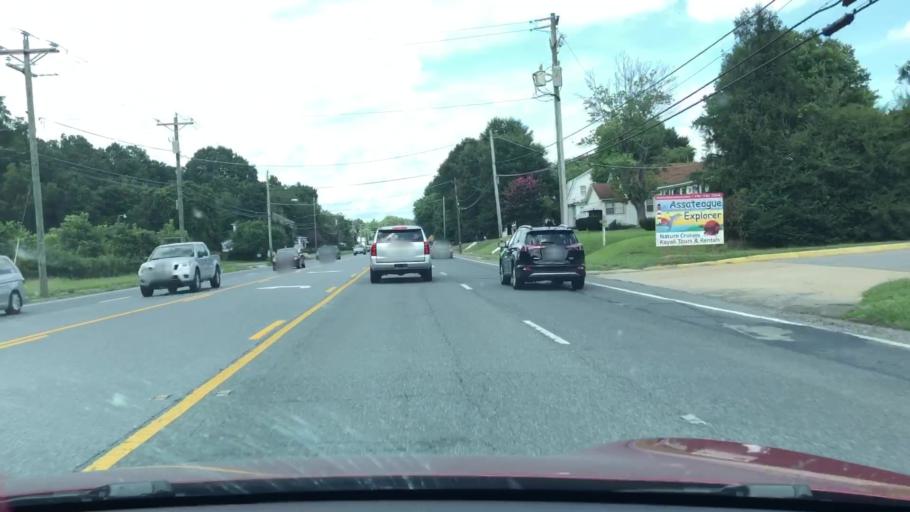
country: US
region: Virginia
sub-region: Accomack County
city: Wattsville
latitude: 37.9331
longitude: -75.5474
